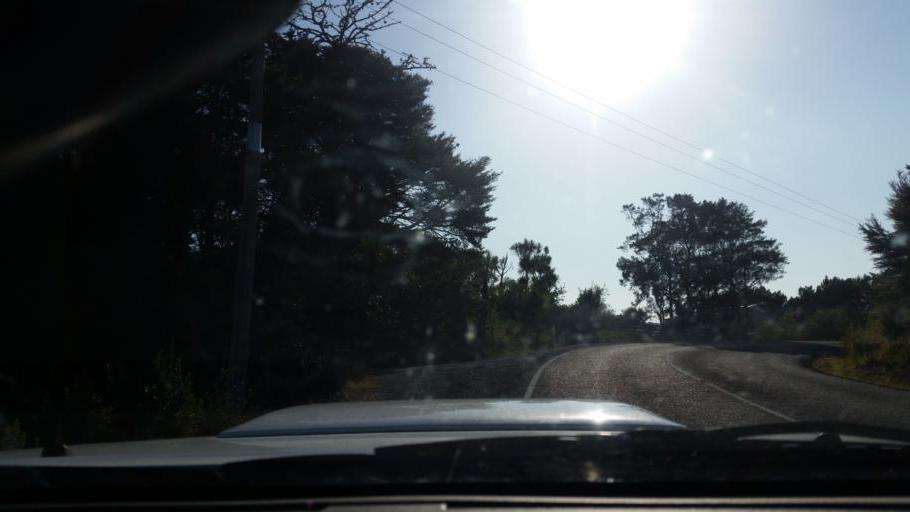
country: NZ
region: Northland
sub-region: Whangarei
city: Ruakaka
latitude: -36.1151
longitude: 174.2297
